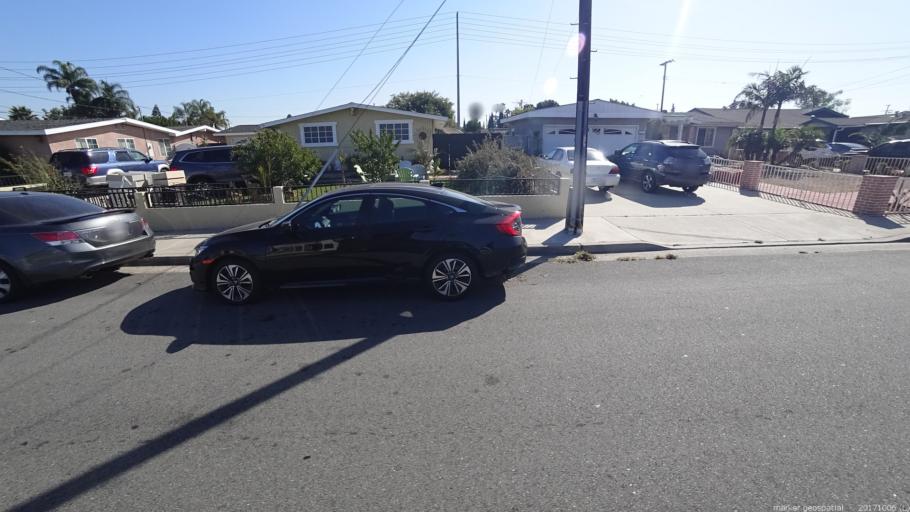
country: US
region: California
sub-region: Orange County
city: Stanton
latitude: 33.7849
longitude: -117.9803
